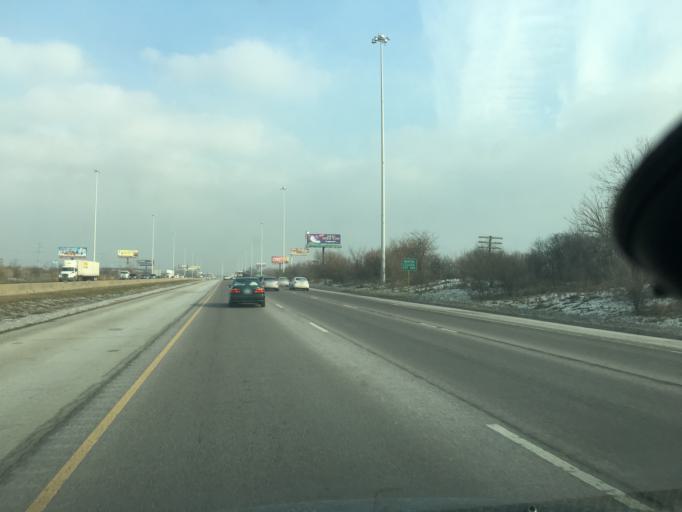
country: US
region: Illinois
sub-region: Cook County
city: Stickney
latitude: 41.8041
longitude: -87.7840
